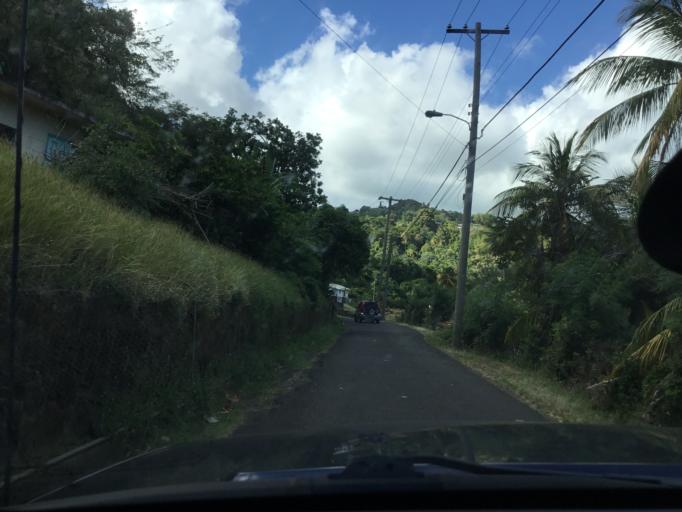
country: VC
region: Saint George
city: Kingstown
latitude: 13.1450
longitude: -61.1743
